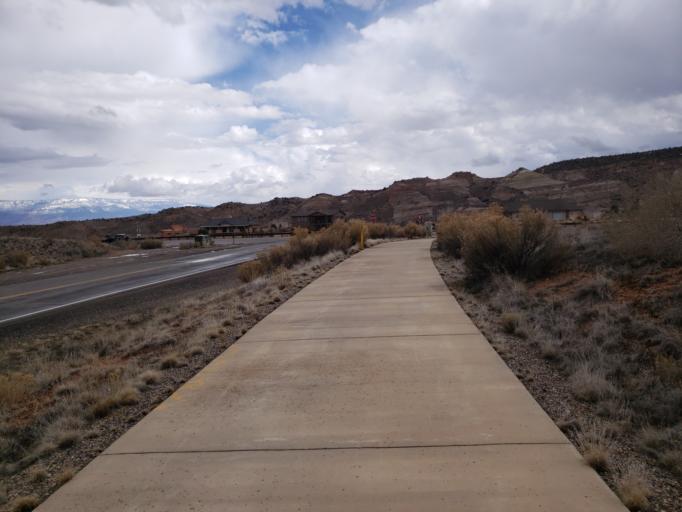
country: US
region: Colorado
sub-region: Mesa County
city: Redlands
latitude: 39.0435
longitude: -108.6262
